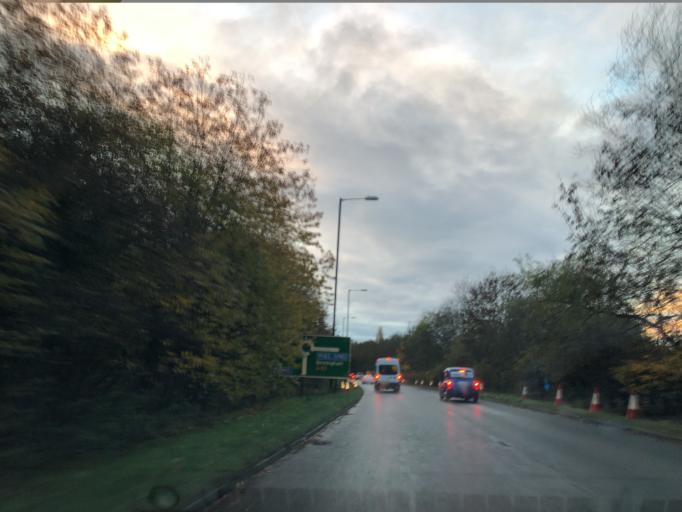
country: GB
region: England
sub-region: Coventry
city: Keresley
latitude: 52.4223
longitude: -1.5659
